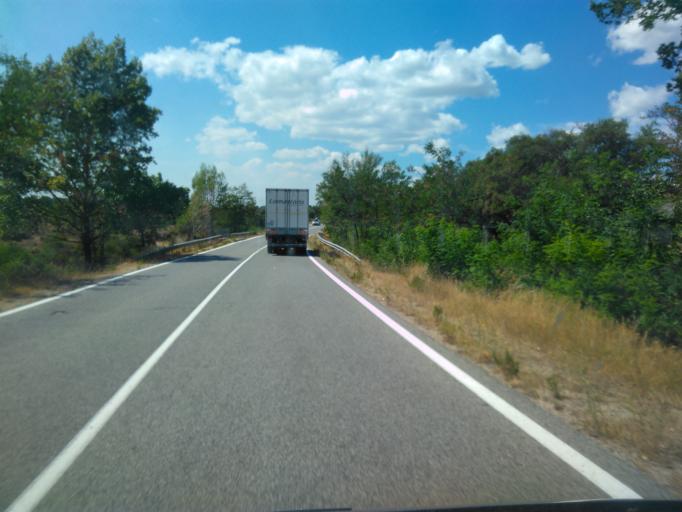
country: FR
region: Provence-Alpes-Cote d'Azur
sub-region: Departement du Var
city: La Garde-Freinet
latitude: 43.3543
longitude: 6.4126
